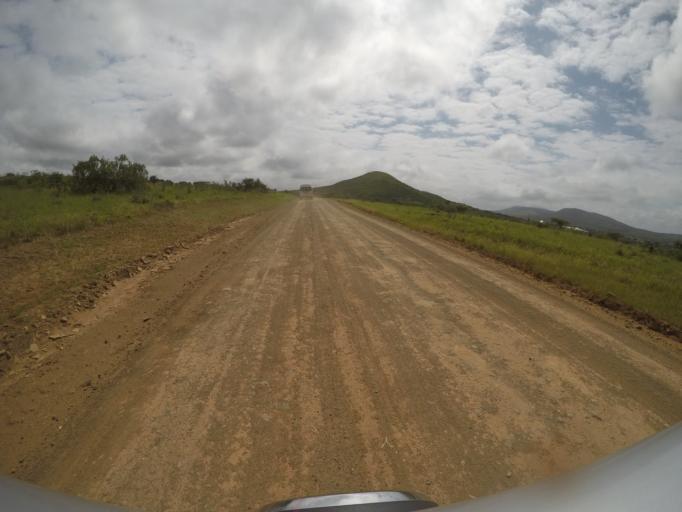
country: ZA
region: KwaZulu-Natal
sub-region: uThungulu District Municipality
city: Empangeni
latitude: -28.6084
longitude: 31.8472
